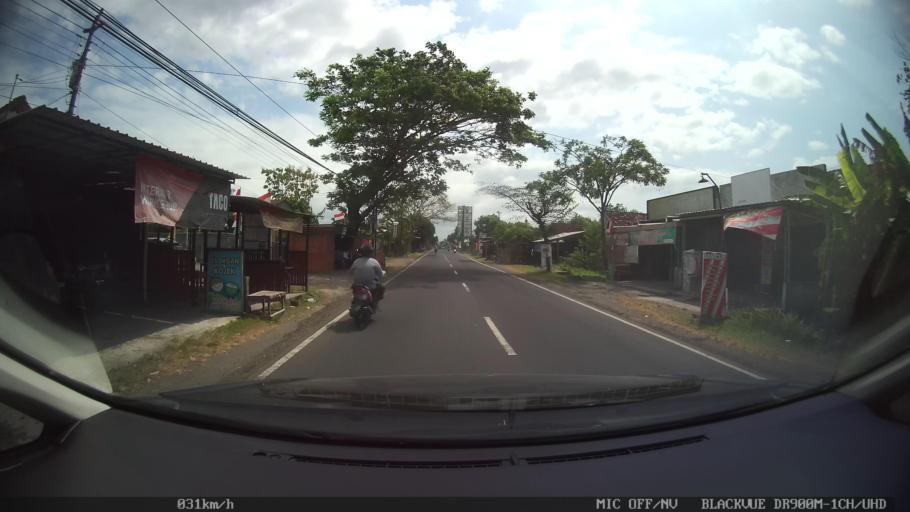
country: ID
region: Central Java
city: Candi Prambanan
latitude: -7.8227
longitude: 110.4799
